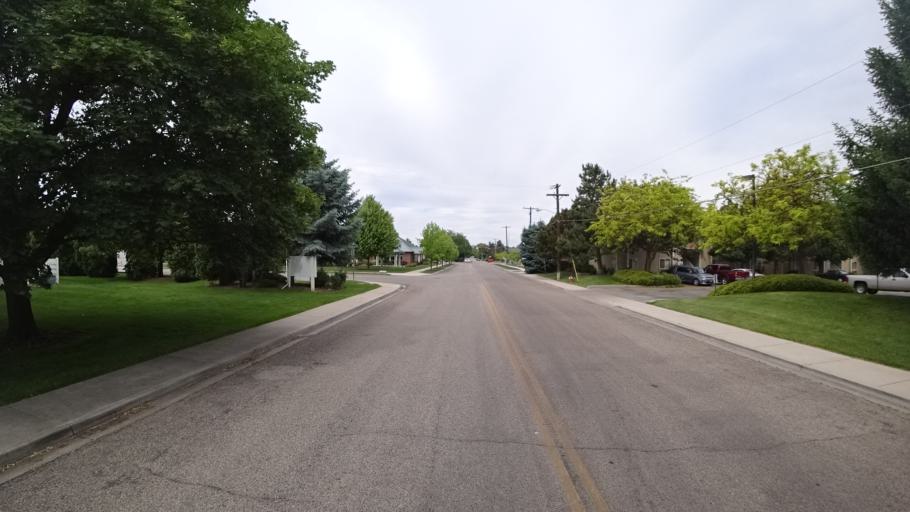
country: US
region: Idaho
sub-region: Ada County
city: Boise
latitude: 43.5771
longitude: -116.2118
